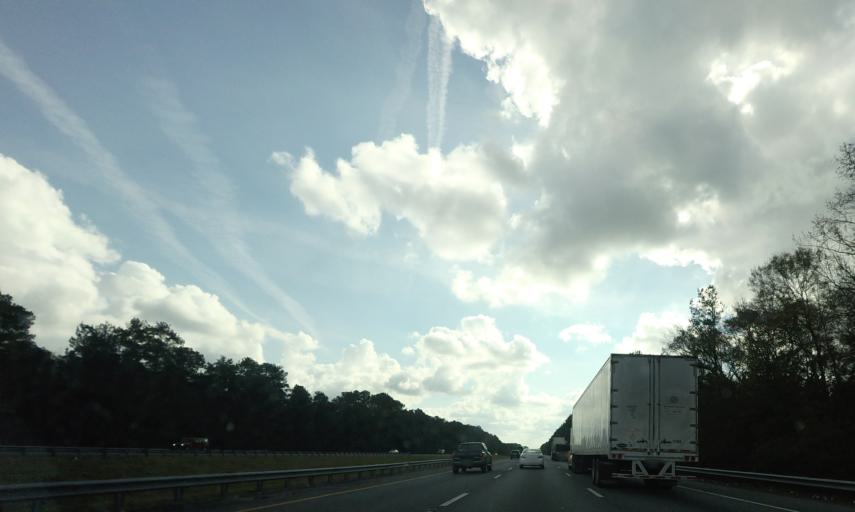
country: US
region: Georgia
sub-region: Houston County
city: Perry
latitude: 32.3730
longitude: -83.7685
